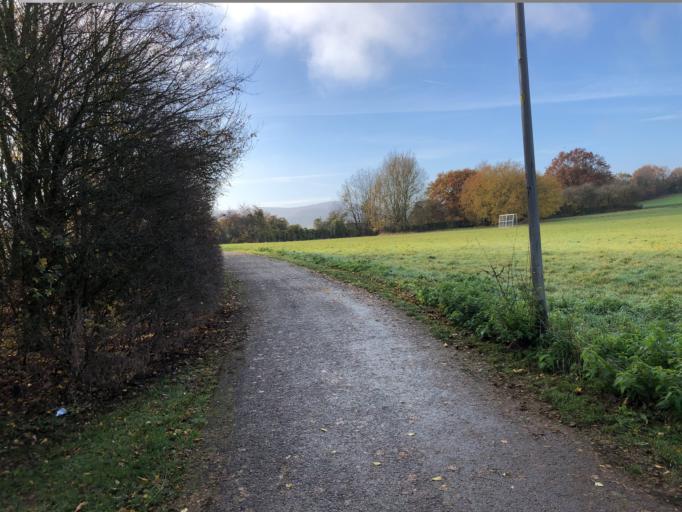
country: DE
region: North Rhine-Westphalia
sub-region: Regierungsbezirk Detmold
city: Detmold
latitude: 51.9334
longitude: 8.8478
